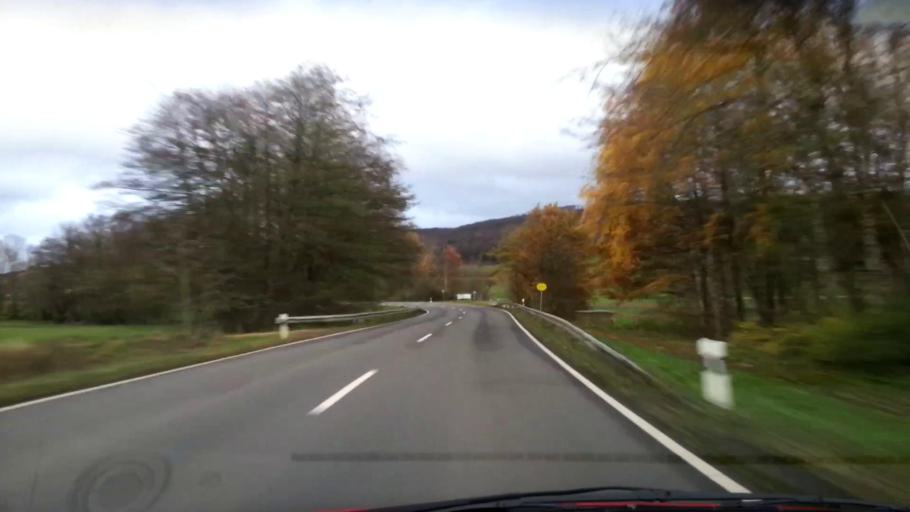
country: DE
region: Bavaria
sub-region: Upper Franconia
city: Litzendorf
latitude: 49.9156
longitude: 11.0356
